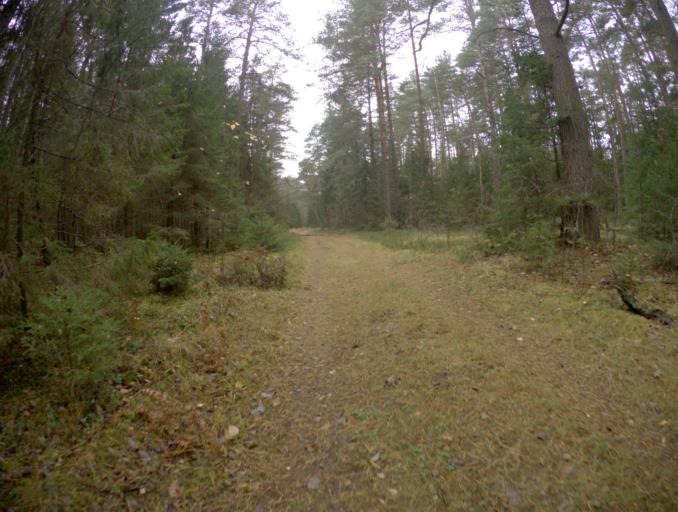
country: RU
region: Vladimir
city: Orgtrud
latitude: 56.1154
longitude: 40.6045
